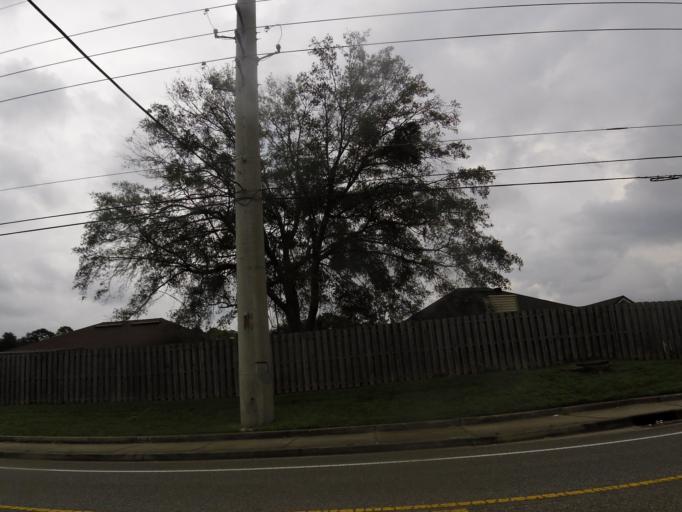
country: US
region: Florida
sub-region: Clay County
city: Bellair-Meadowbrook Terrace
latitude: 30.2051
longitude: -81.7647
